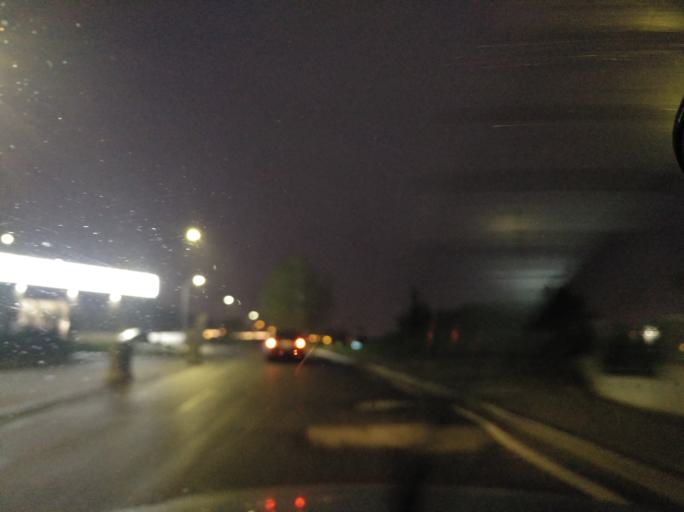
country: PT
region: Lisbon
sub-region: Loures
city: Apelacao
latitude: 38.8161
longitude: -9.1473
